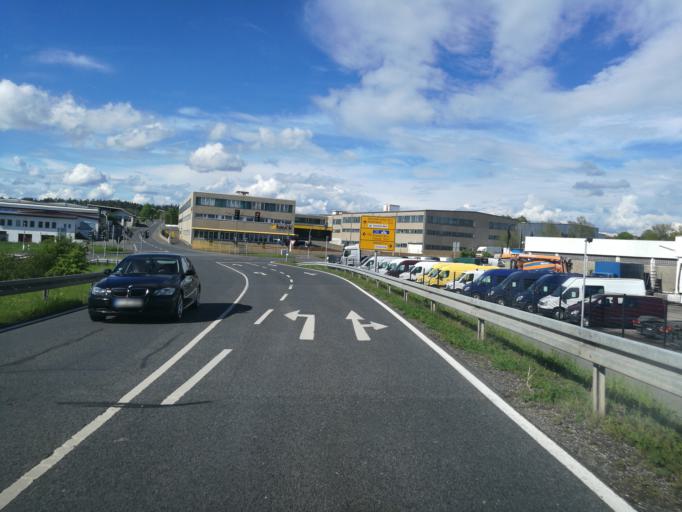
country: DE
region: Bavaria
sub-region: Upper Franconia
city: Sonnefeld
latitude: 50.2191
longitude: 11.1235
